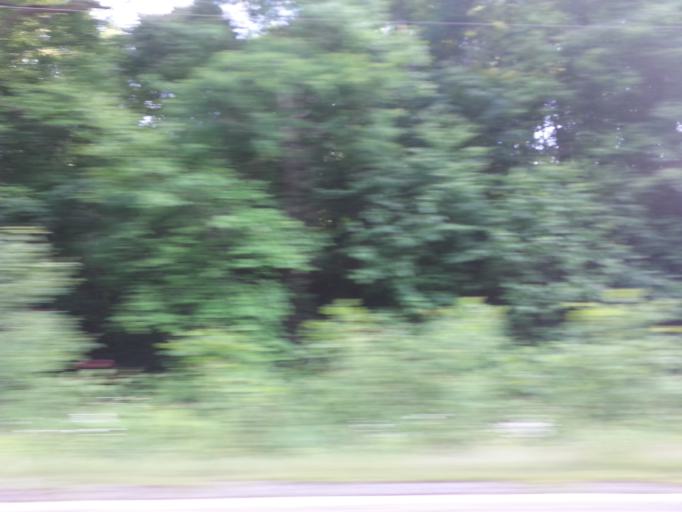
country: US
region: Georgia
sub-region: Union County
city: Blairsville
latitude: 34.8098
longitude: -83.8400
